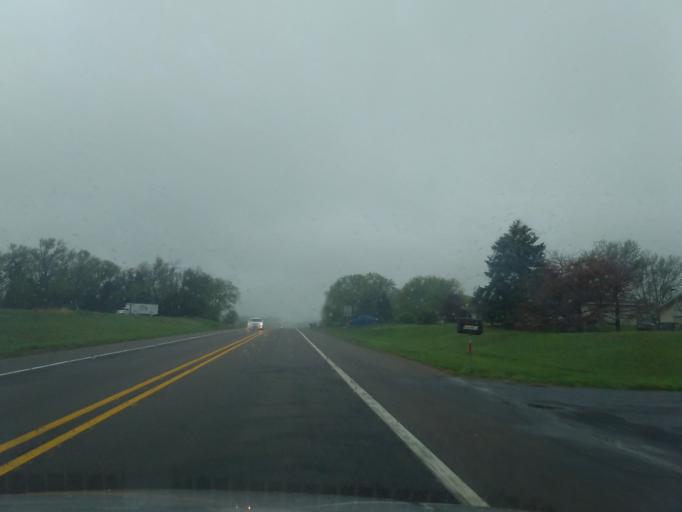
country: US
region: Nebraska
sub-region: Madison County
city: Norfolk
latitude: 42.0745
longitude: -97.3325
